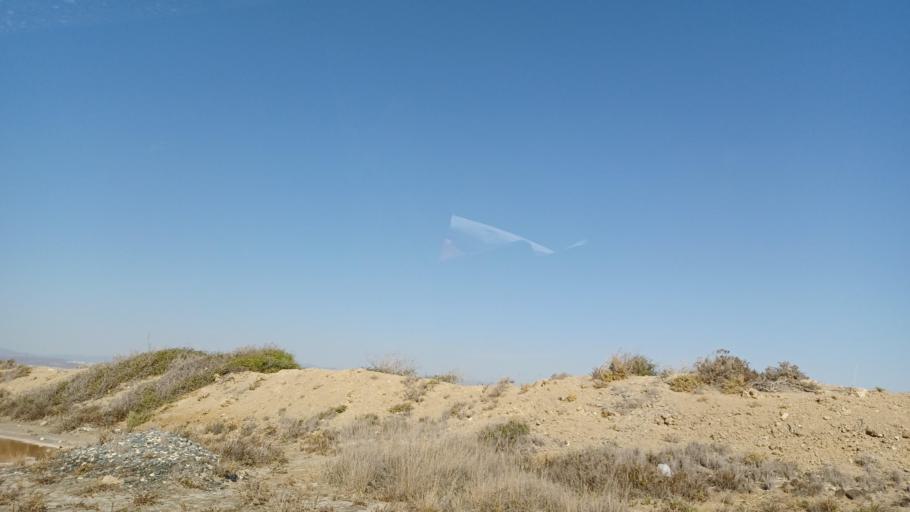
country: CY
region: Larnaka
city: Kolossi
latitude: 34.6049
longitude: 32.9310
